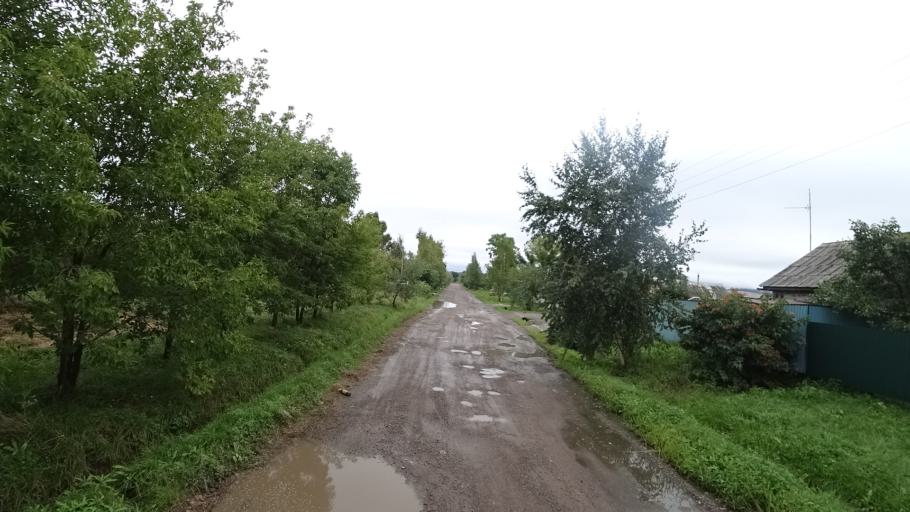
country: RU
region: Primorskiy
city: Monastyrishche
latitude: 44.1962
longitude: 132.4713
